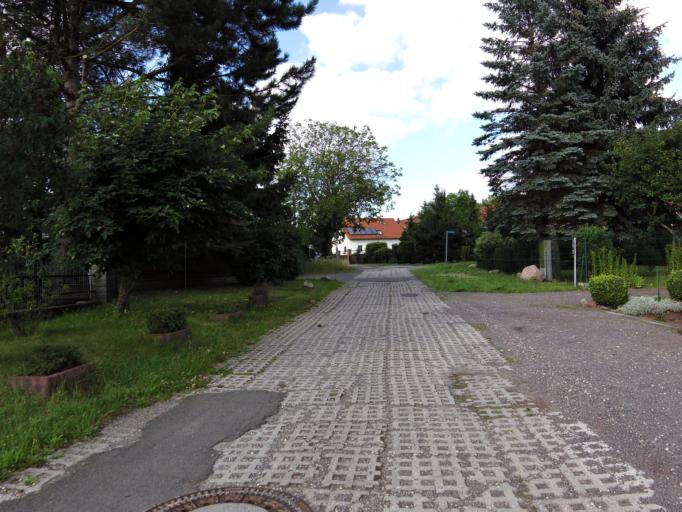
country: DE
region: Saxony
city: Taucha
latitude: 51.3340
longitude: 12.4393
